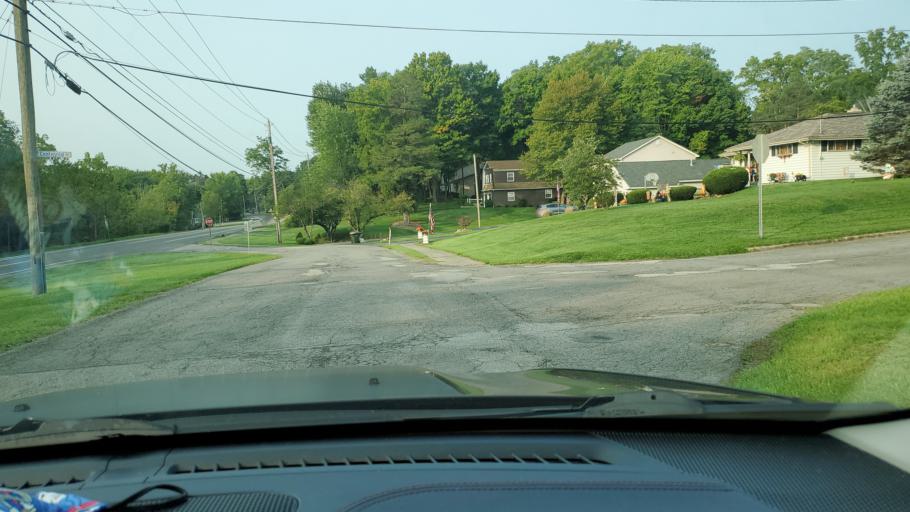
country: US
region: Ohio
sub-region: Mahoning County
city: Poland
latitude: 41.0290
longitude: -80.6081
